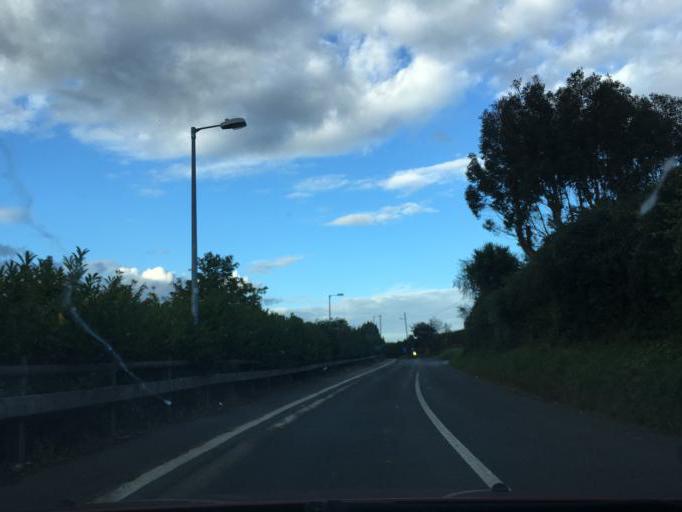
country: IE
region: Leinster
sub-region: Wicklow
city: Wicklow
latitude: 52.9699
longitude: -6.0578
